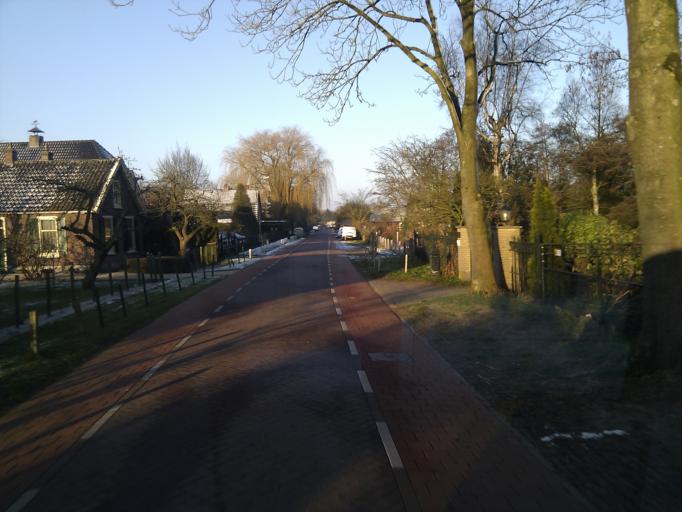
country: NL
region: Utrecht
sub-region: Stichtse Vecht
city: Maarssen
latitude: 52.1439
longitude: 5.0926
